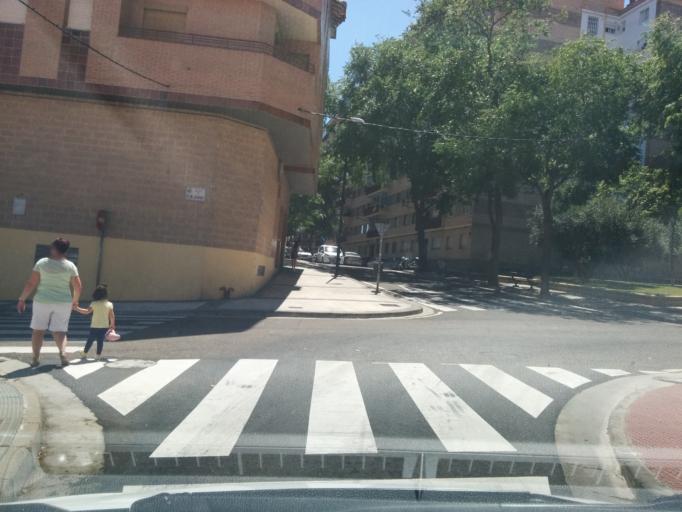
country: ES
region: Aragon
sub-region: Provincia de Zaragoza
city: Zaragoza
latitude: 41.6265
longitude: -0.8762
